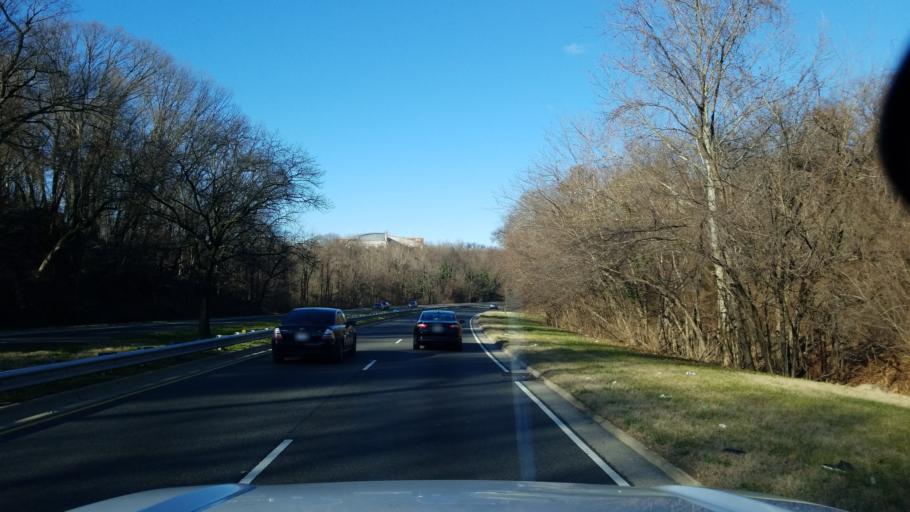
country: US
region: Maryland
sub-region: Prince George's County
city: Glassmanor
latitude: 38.8530
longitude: -76.9893
